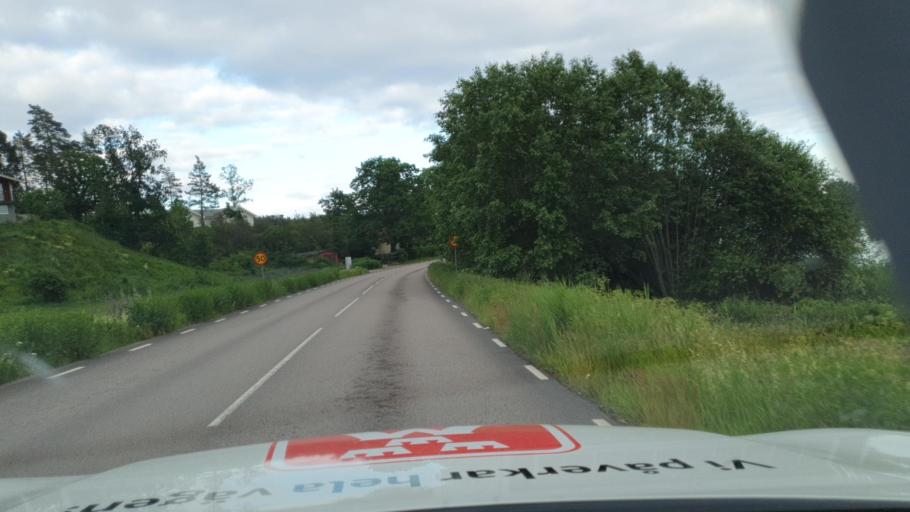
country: SE
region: Vaermland
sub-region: Karlstads Kommun
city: Karlstad
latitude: 59.4235
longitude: 13.4800
